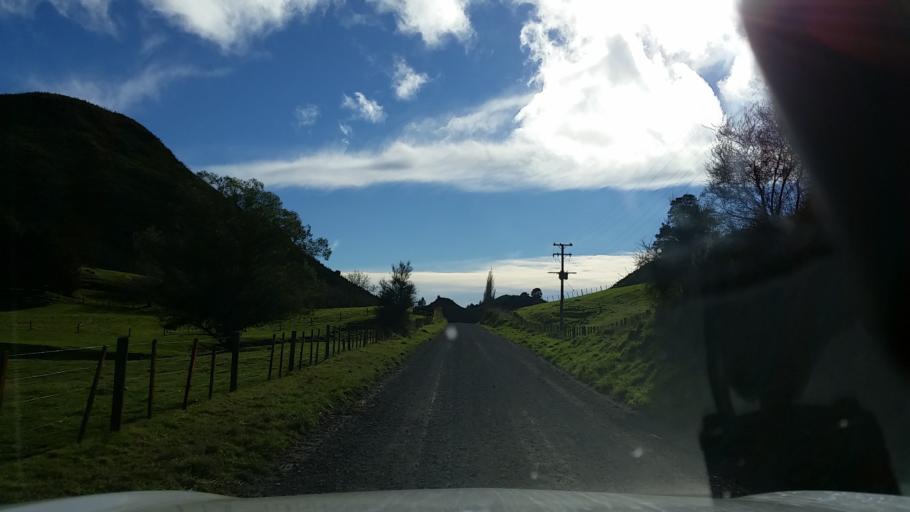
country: NZ
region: Bay of Plenty
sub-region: Rotorua District
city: Rotorua
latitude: -38.3660
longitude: 176.2076
